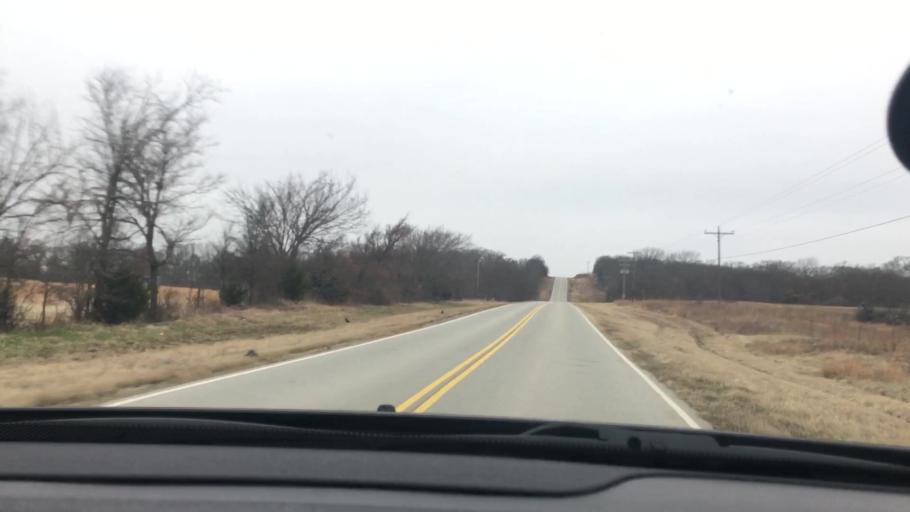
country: US
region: Oklahoma
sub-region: Coal County
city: Coalgate
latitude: 34.5057
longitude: -96.3119
